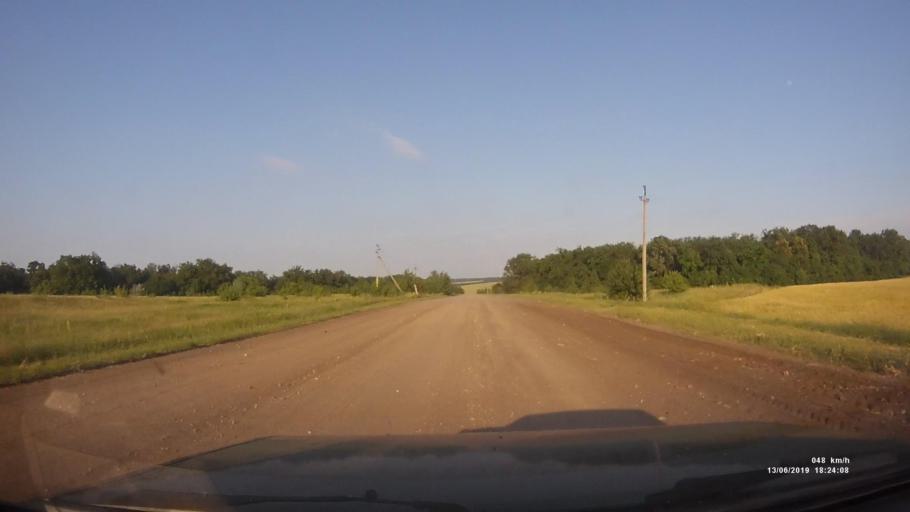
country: RU
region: Rostov
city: Kazanskaya
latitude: 49.8522
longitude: 41.2866
